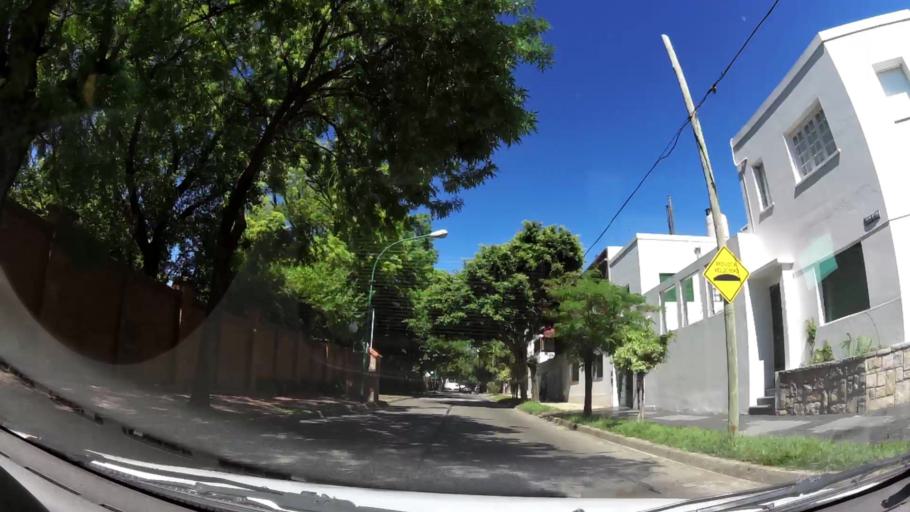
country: AR
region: Buenos Aires
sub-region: Partido de Vicente Lopez
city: Olivos
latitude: -34.5152
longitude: -58.4865
